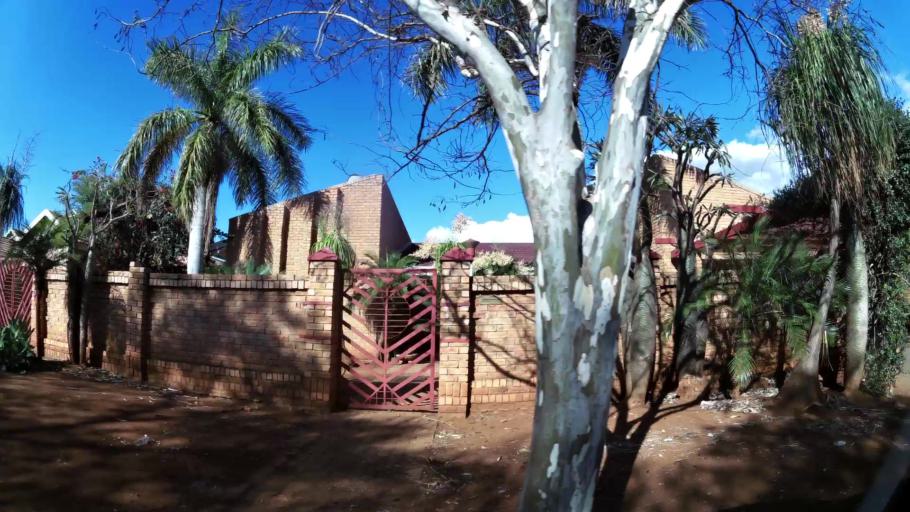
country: ZA
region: Limpopo
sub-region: Waterberg District Municipality
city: Mokopane
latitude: -24.1811
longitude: 28.9970
